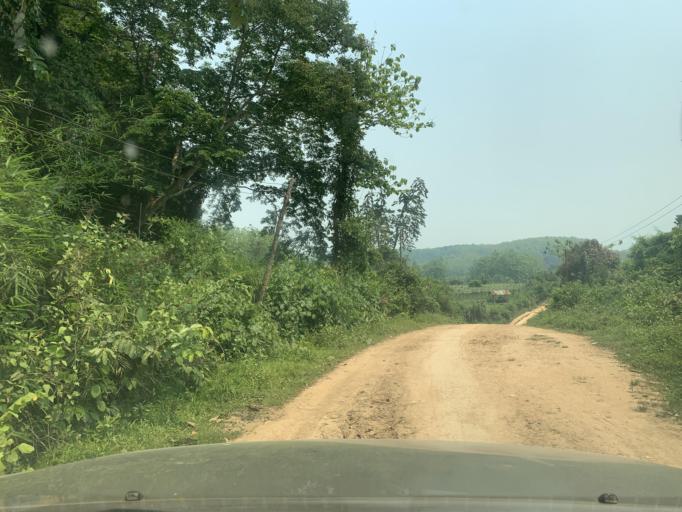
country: LA
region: Louangphabang
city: Xiang Ngeun
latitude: 19.8231
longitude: 102.2110
